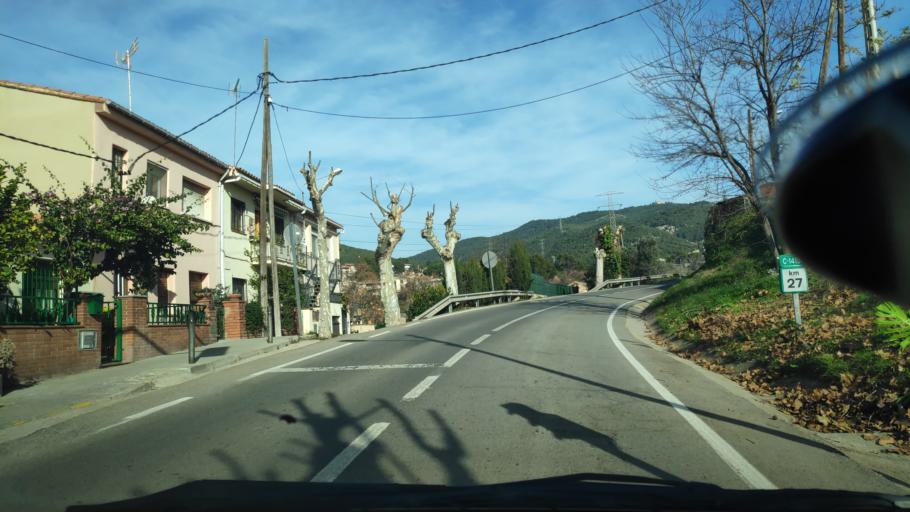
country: ES
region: Catalonia
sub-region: Provincia de Barcelona
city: Castellar del Valles
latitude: 41.6148
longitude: 2.0801
